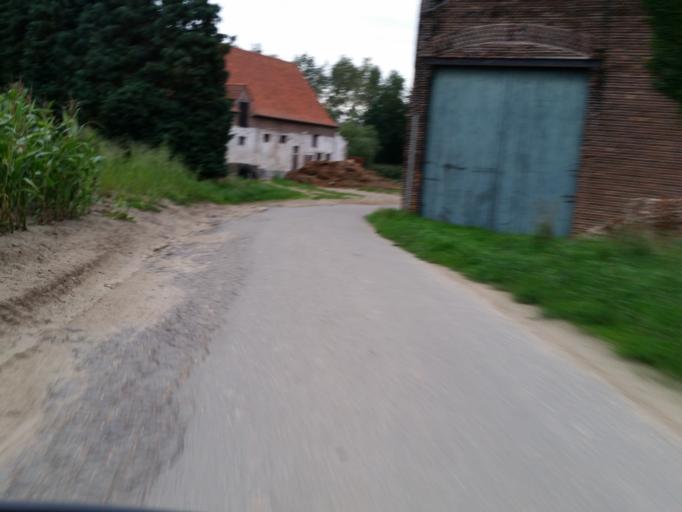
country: BE
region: Flanders
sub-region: Provincie Vlaams-Brabant
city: Zemst
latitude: 50.9878
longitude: 4.4596
